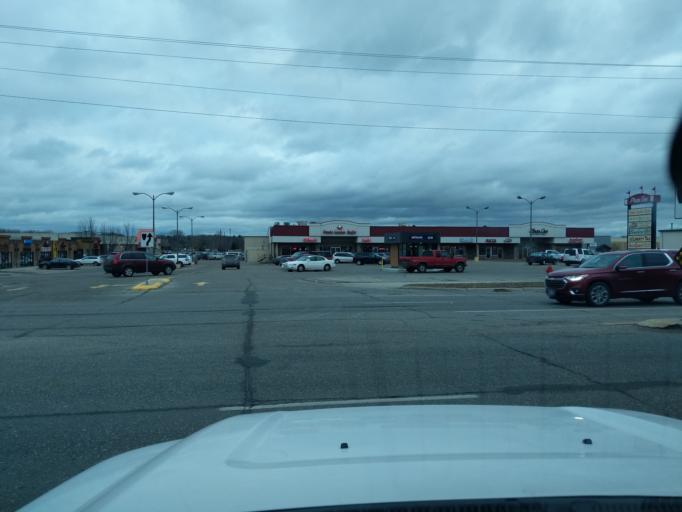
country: US
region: Minnesota
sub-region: Kandiyohi County
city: Willmar
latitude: 45.1093
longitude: -95.0430
